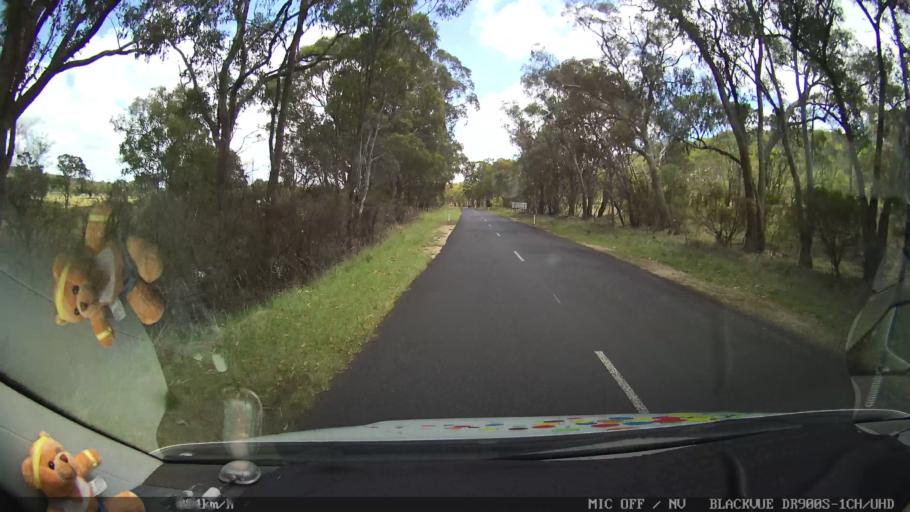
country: AU
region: New South Wales
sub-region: Glen Innes Severn
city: Glen Innes
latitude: -29.5343
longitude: 151.6735
